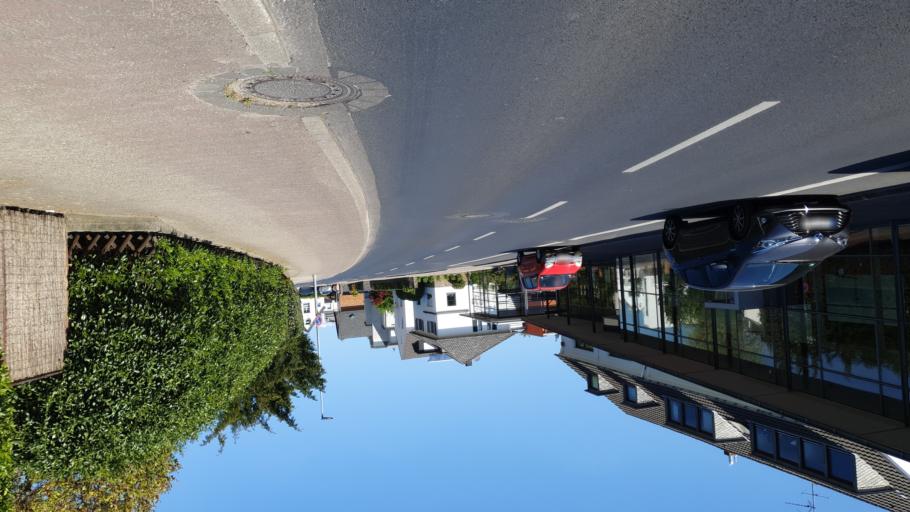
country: DE
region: North Rhine-Westphalia
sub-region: Regierungsbezirk Koln
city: Odenthal
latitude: 51.0120
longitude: 7.0810
